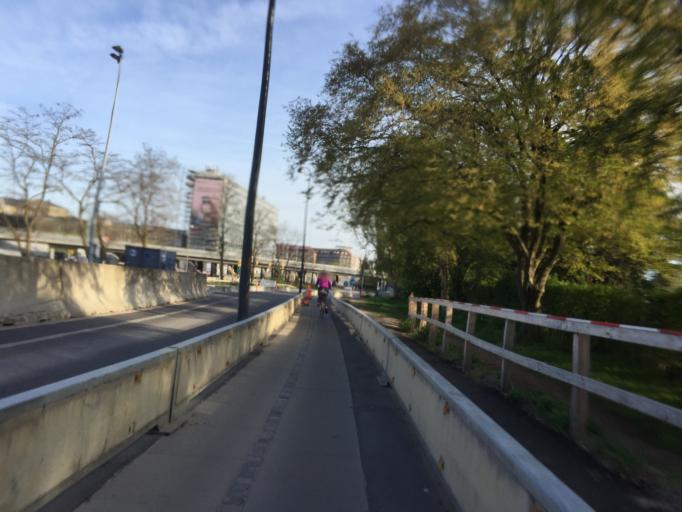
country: DK
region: Capital Region
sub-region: Kobenhavn
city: Copenhagen
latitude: 55.7164
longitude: 12.5574
